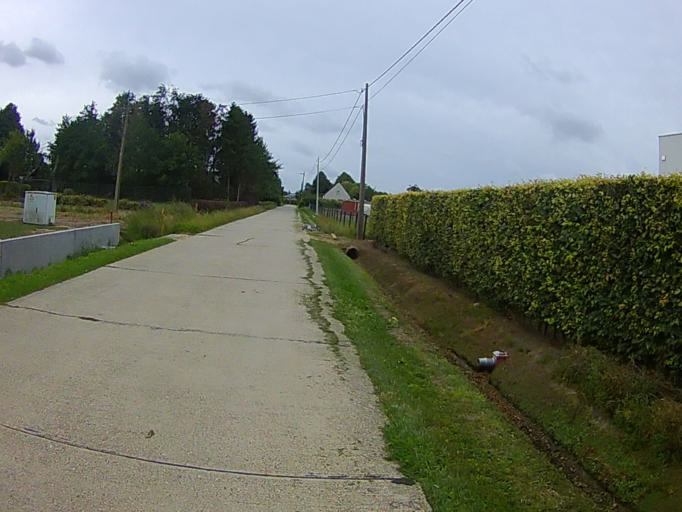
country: BE
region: Flanders
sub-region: Provincie Antwerpen
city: Ranst
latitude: 51.1800
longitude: 4.5807
